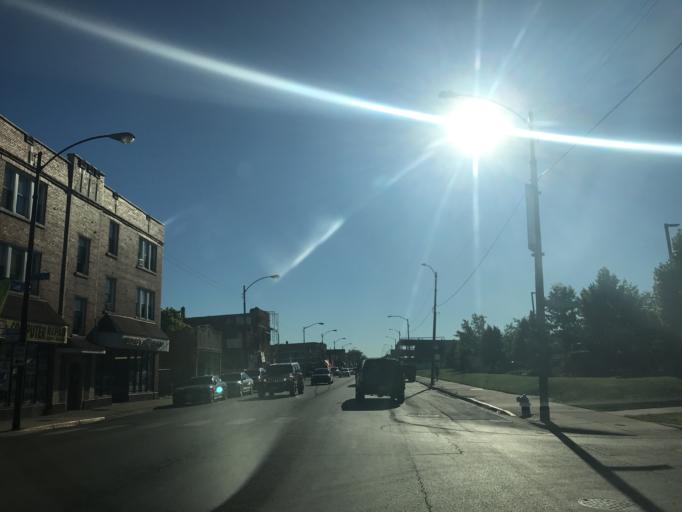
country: US
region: Illinois
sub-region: Cook County
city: Cicero
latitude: 41.8656
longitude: -87.7665
